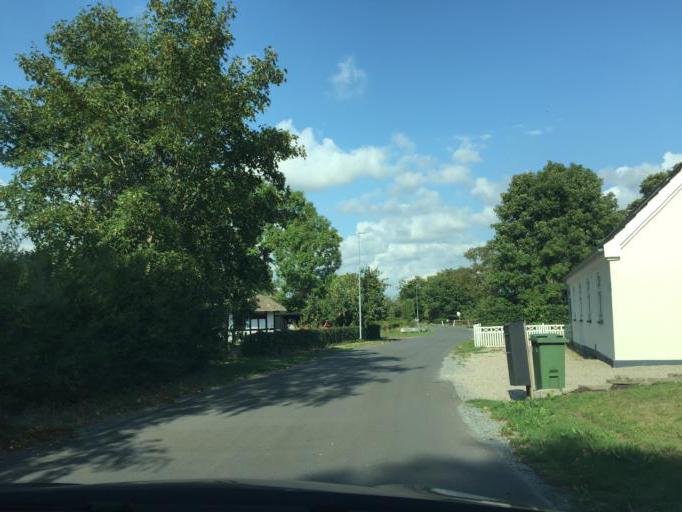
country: DK
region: South Denmark
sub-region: Odense Kommune
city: Bellinge
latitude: 55.3100
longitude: 10.3753
